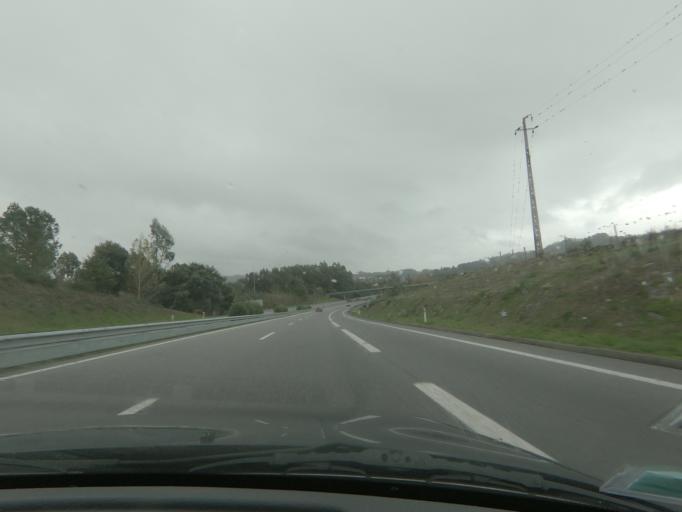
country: PT
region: Porto
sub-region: Lousada
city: Meinedo
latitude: 41.2358
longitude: -8.1964
